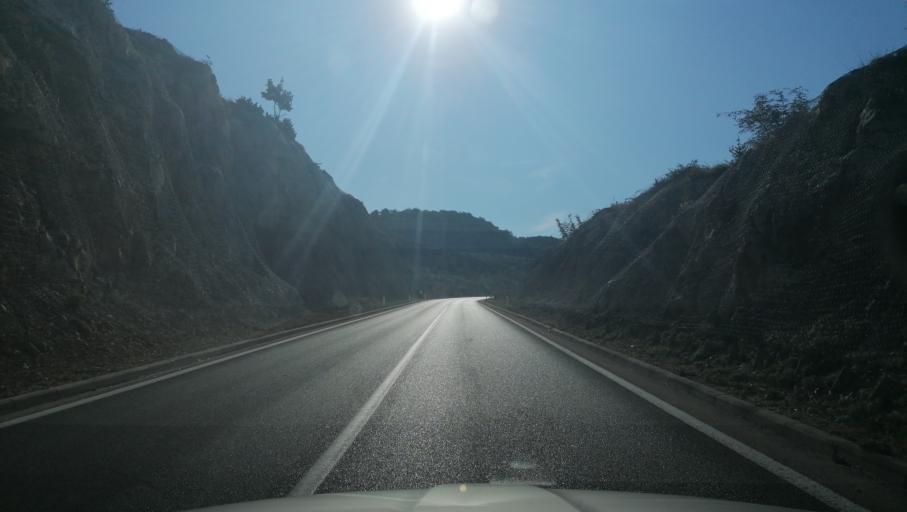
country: BA
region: Republika Srpska
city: Trebinje
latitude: 42.6749
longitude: 18.3437
